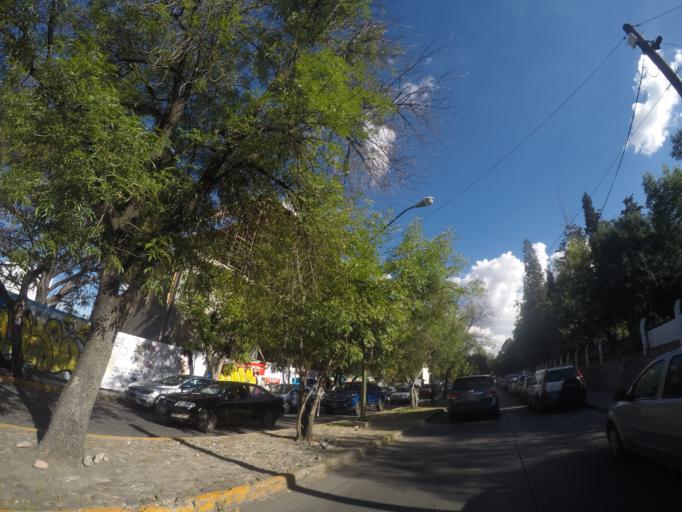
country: MX
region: San Luis Potosi
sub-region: San Luis Potosi
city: San Luis Potosi
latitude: 22.1480
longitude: -101.0189
